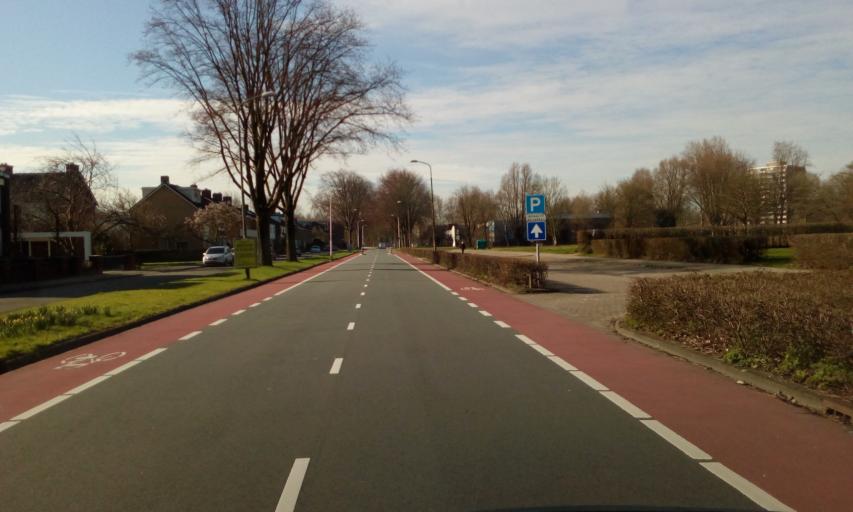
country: NL
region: South Holland
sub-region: Gemeente Zoetermeer
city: Zoetermeer
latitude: 52.0524
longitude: 4.4924
